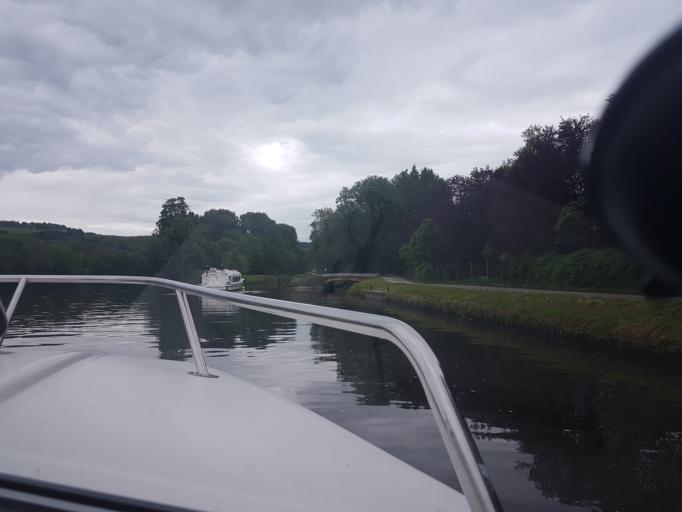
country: FR
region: Bourgogne
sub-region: Departement de l'Yonne
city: Champs-sur-Yonne
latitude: 47.7243
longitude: 3.6147
